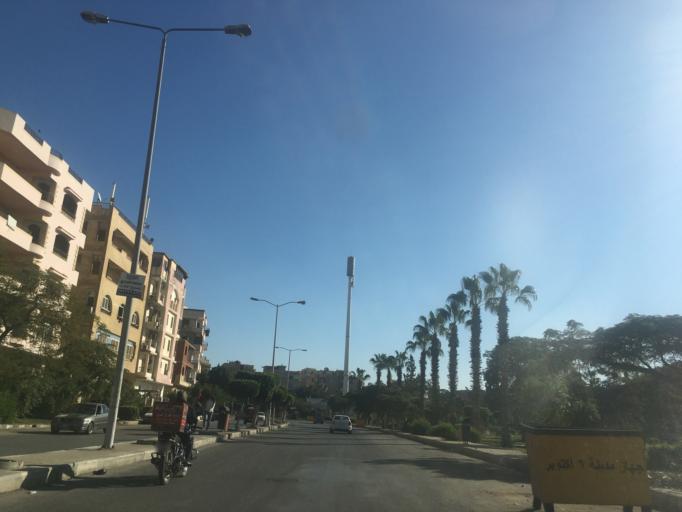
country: EG
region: Al Jizah
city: Madinat Sittah Uktubar
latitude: 29.9825
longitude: 30.9452
